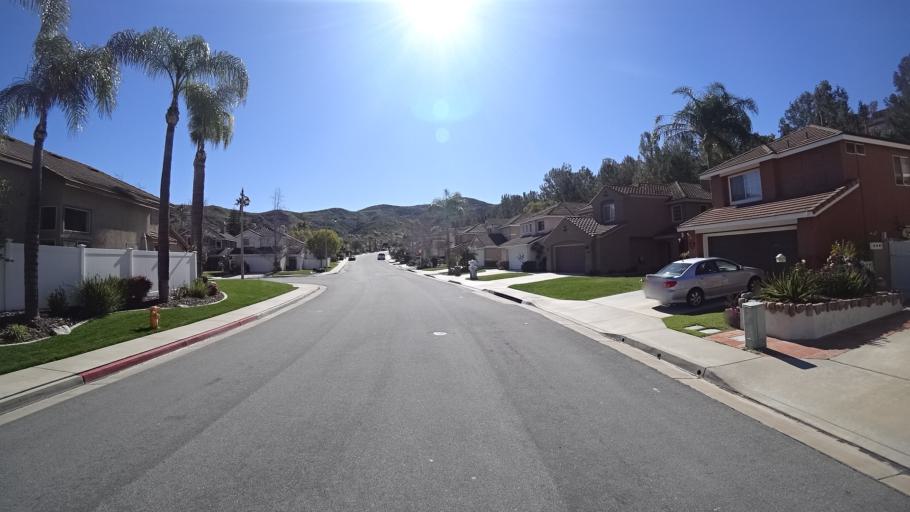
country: US
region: California
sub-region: Orange County
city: Yorba Linda
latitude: 33.8530
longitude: -117.7287
